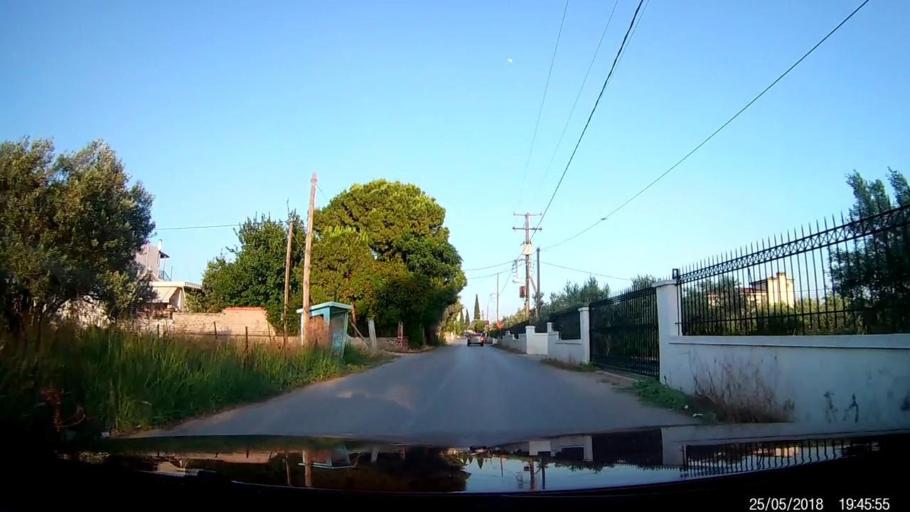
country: GR
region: Central Greece
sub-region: Nomos Evvoias
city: Ayios Nikolaos
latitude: 38.4295
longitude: 23.6368
